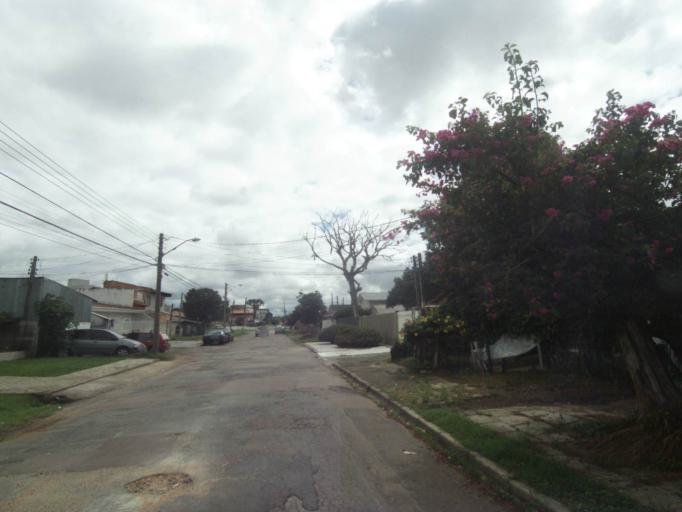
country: BR
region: Parana
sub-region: Curitiba
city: Curitiba
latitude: -25.4783
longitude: -49.2699
